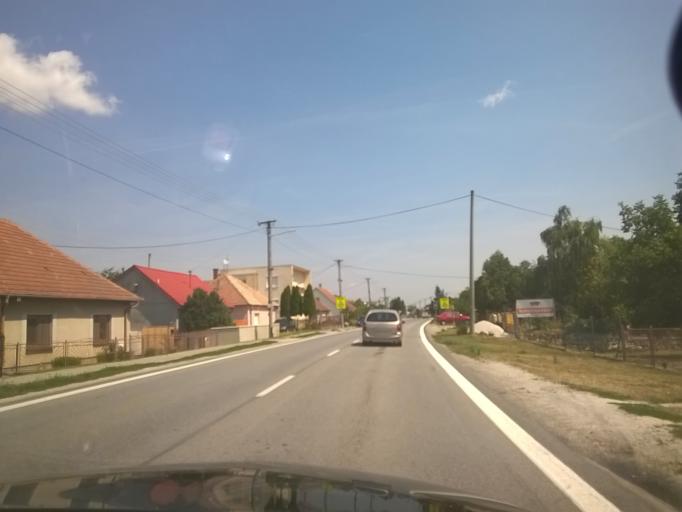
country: SK
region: Nitriansky
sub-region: Okres Nitra
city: Nitra
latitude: 48.4071
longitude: 18.0785
